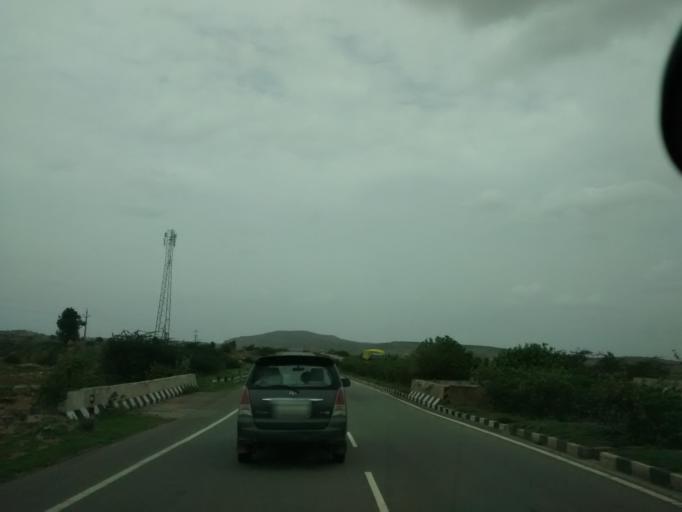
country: IN
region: Andhra Pradesh
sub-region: Kurnool
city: Ramapuram
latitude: 15.2585
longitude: 77.7600
